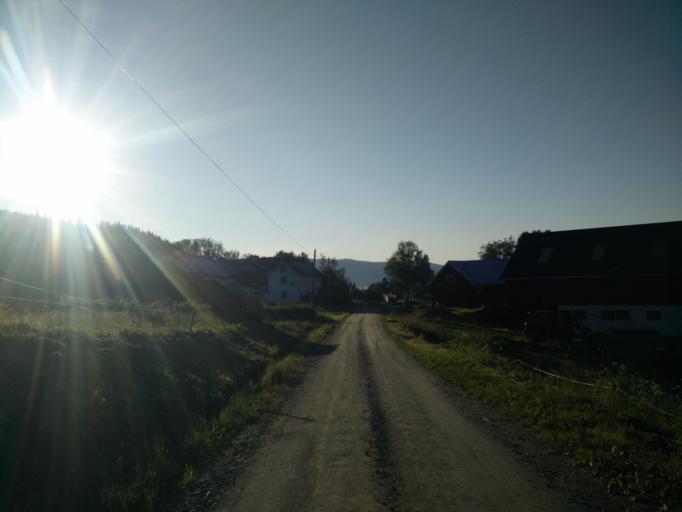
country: NO
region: Sor-Trondelag
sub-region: Skaun
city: Borsa
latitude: 63.3399
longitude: 10.0367
